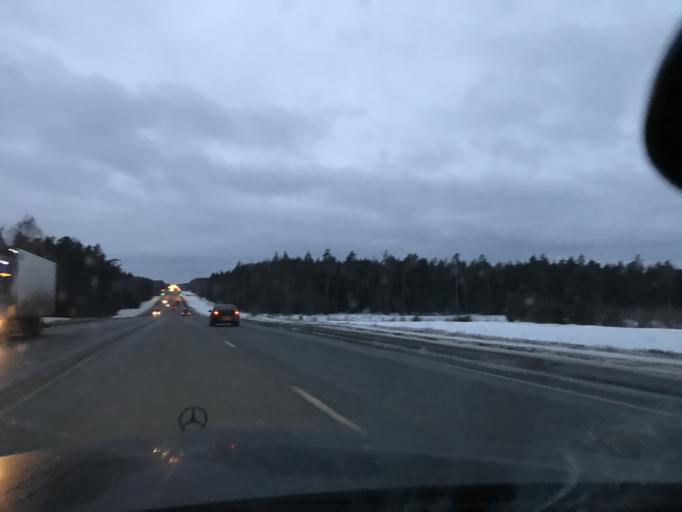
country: RU
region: Vladimir
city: Pokrov
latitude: 55.9254
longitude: 39.2818
